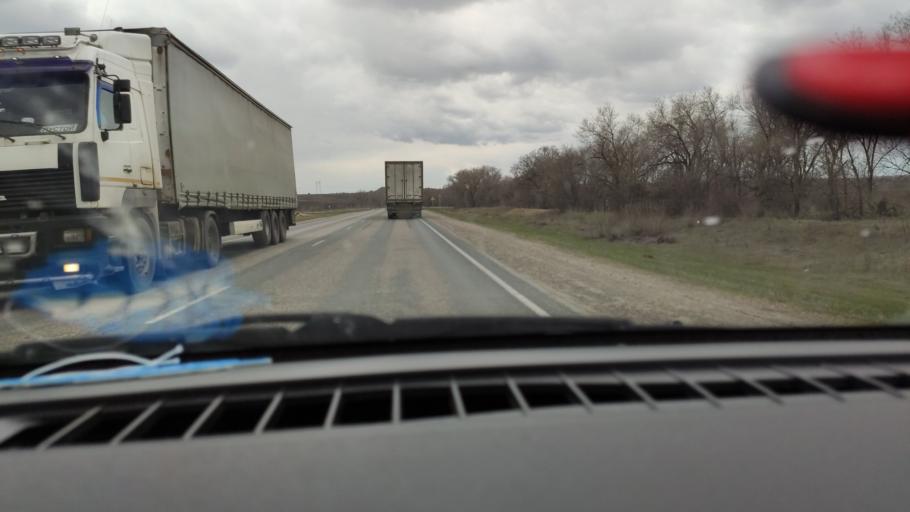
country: RU
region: Saratov
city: Sinodskoye
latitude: 51.9676
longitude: 46.6360
